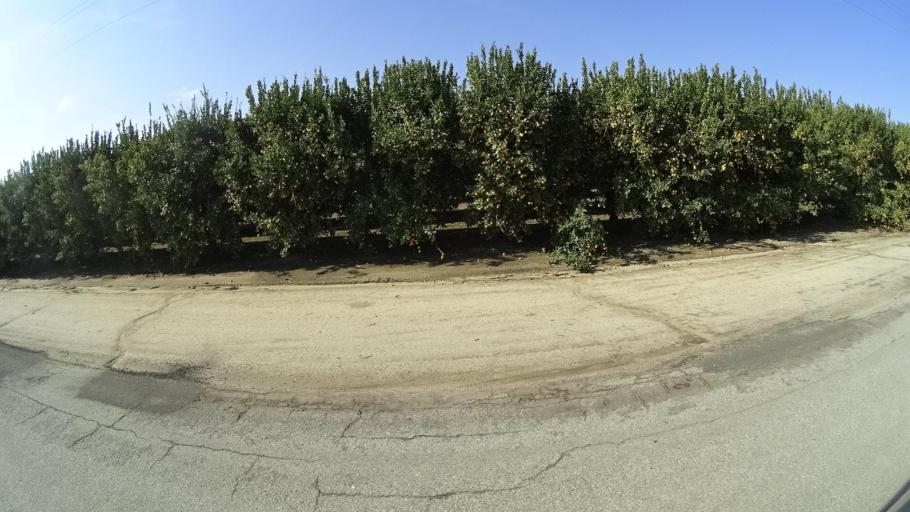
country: US
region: California
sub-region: Kern County
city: Arvin
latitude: 35.2926
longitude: -118.7709
